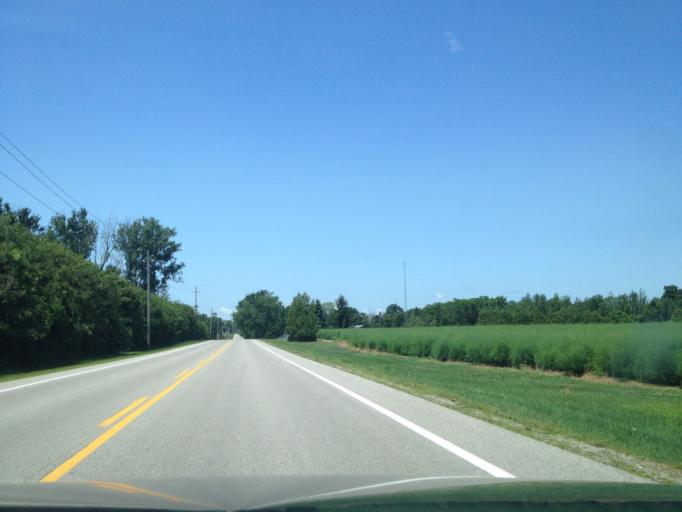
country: CA
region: Ontario
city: Norfolk County
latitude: 42.5949
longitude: -80.6443
